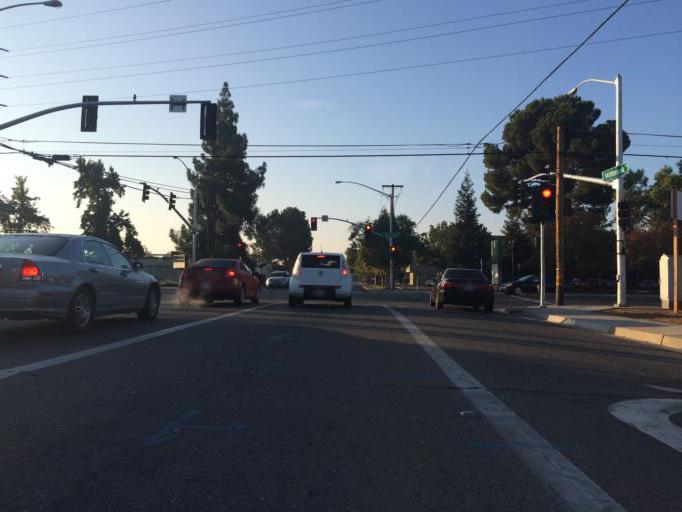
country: US
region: California
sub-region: Fresno County
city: Fresno
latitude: 36.7800
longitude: -119.7635
